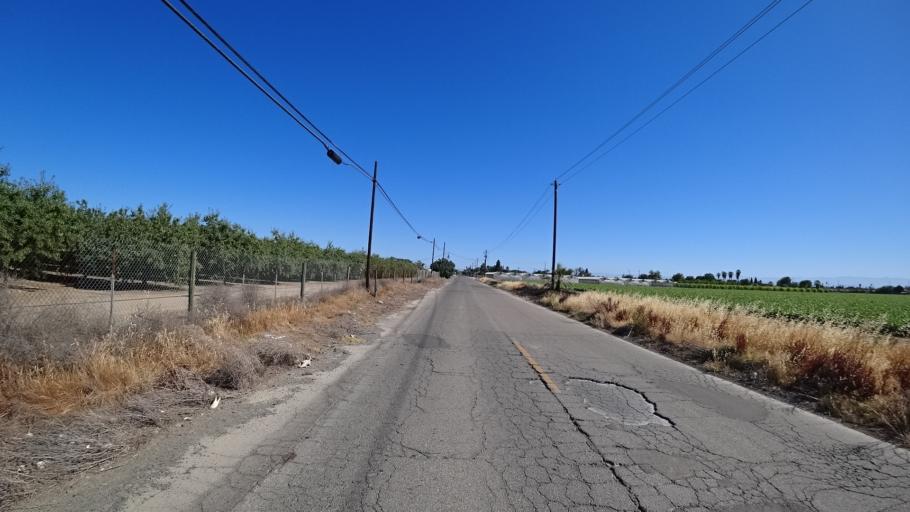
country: US
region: California
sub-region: Fresno County
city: West Park
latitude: 36.7035
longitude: -119.8089
